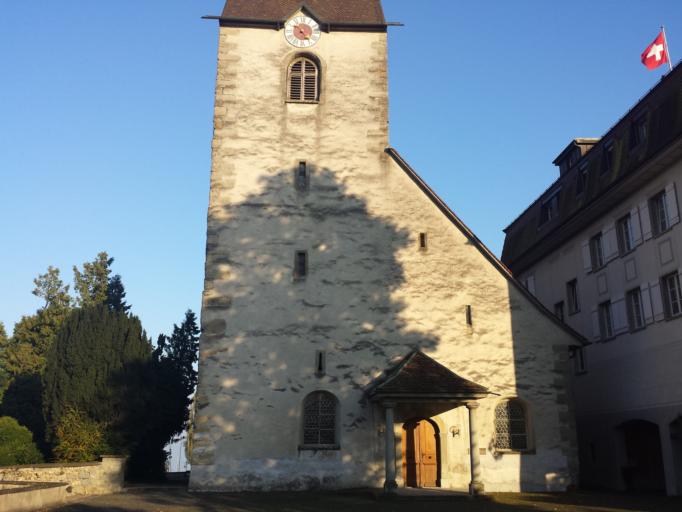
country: CH
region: Thurgau
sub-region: Arbon District
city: Romanshorn
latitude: 47.5688
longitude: 9.3817
